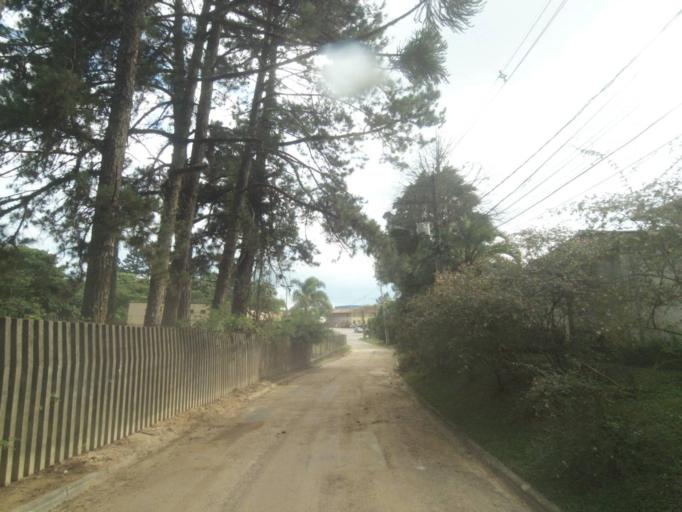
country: BR
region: Parana
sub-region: Curitiba
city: Curitiba
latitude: -25.4506
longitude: -49.3584
